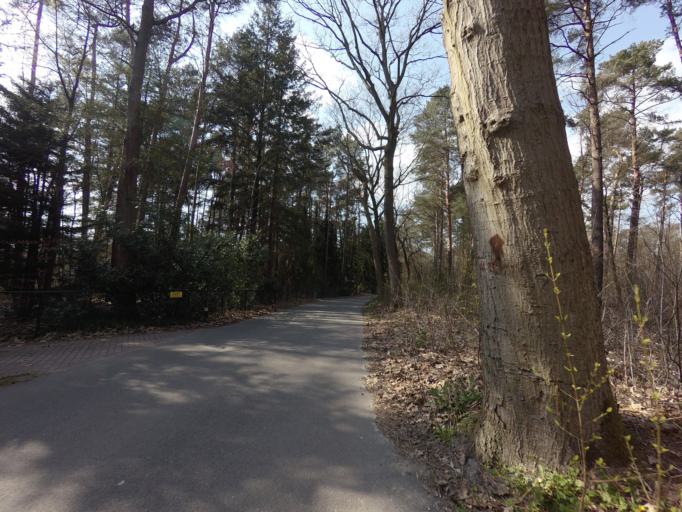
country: NL
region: Gelderland
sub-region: Gemeente Nunspeet
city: Nunspeet
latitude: 52.3601
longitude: 5.7436
